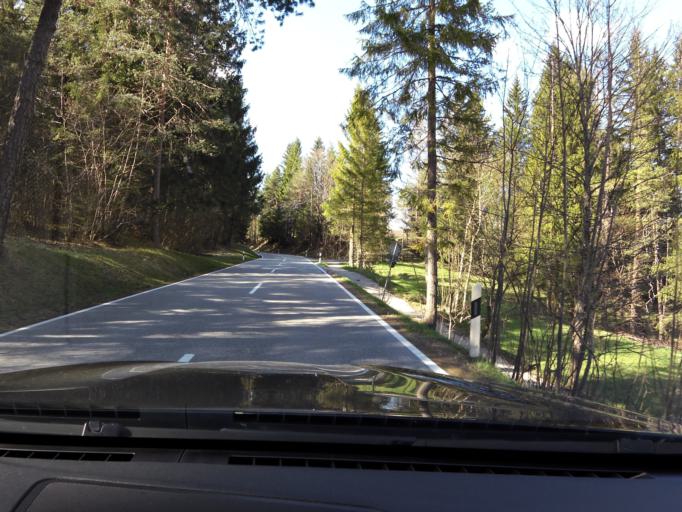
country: DE
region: Bavaria
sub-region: Upper Bavaria
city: Mittenwald
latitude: 47.4672
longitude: 11.2597
